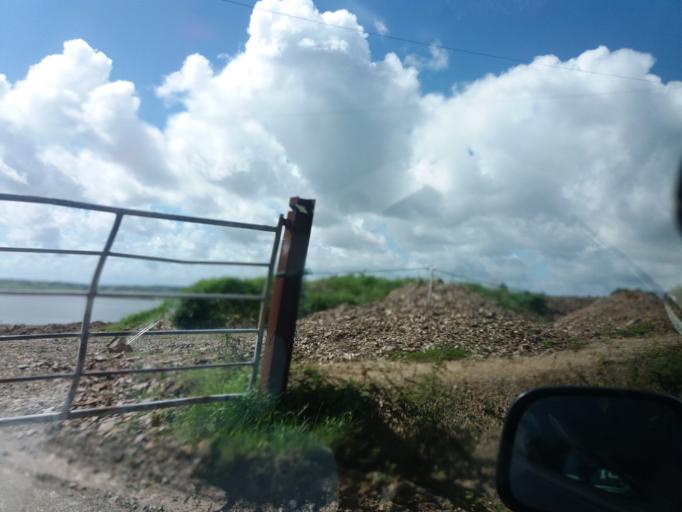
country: IE
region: Munster
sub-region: Waterford
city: Dunmore East
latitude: 52.2280
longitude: -6.9334
